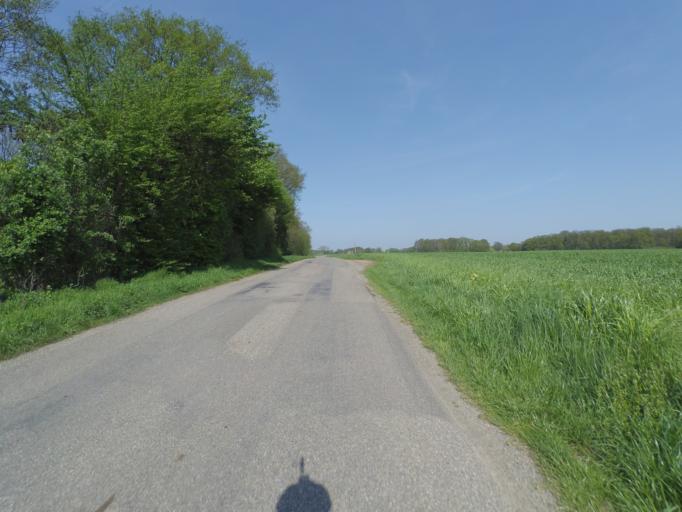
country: DE
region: North Rhine-Westphalia
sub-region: Regierungsbezirk Munster
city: Isselburg
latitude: 51.8014
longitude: 6.4572
